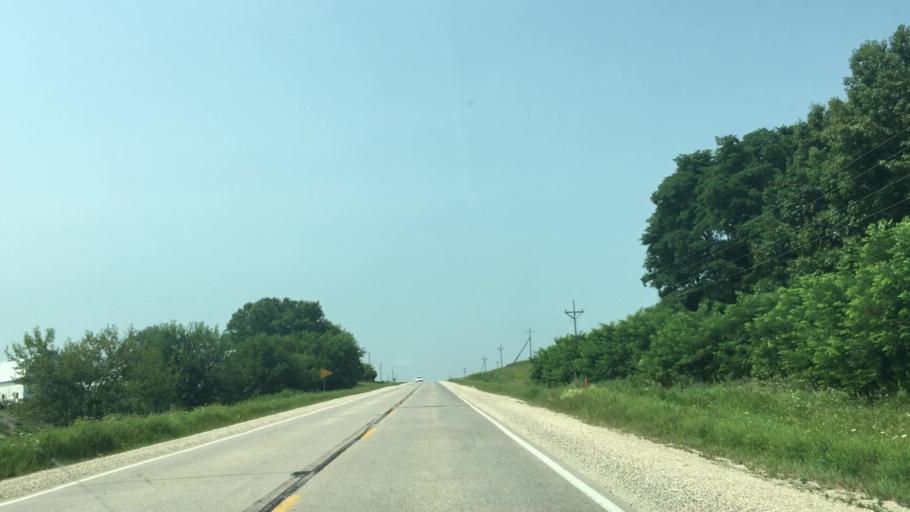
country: US
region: Iowa
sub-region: Fayette County
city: West Union
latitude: 43.0863
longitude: -91.8491
